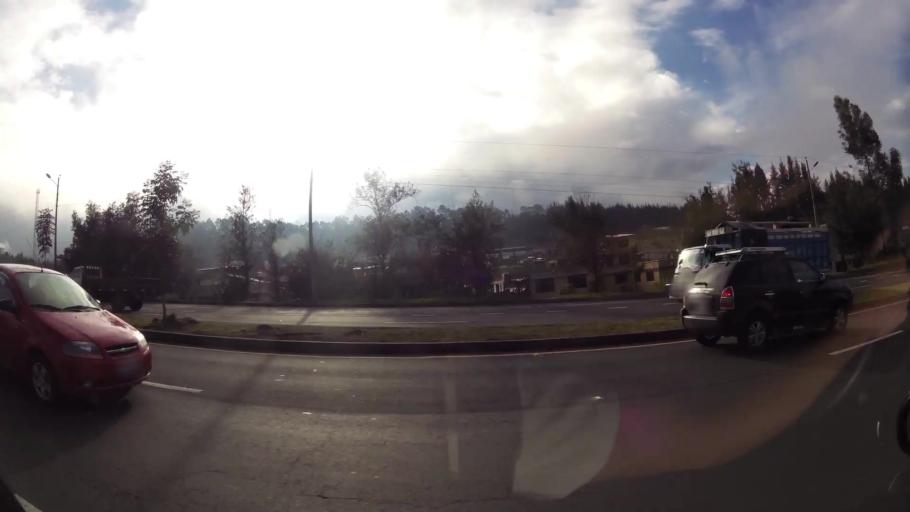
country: EC
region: Pichincha
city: Quito
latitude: -0.2411
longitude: -78.4944
